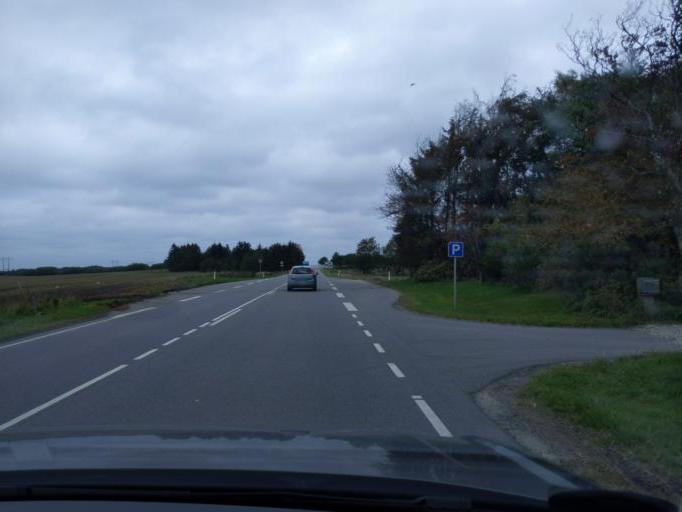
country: DK
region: North Denmark
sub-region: Mariagerfjord Kommune
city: Hobro
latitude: 56.5760
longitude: 9.8147
